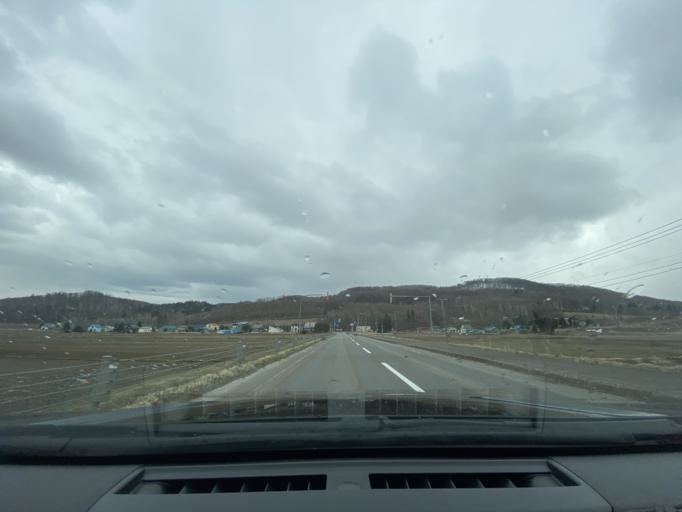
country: JP
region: Hokkaido
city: Nayoro
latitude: 44.1700
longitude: 142.2680
